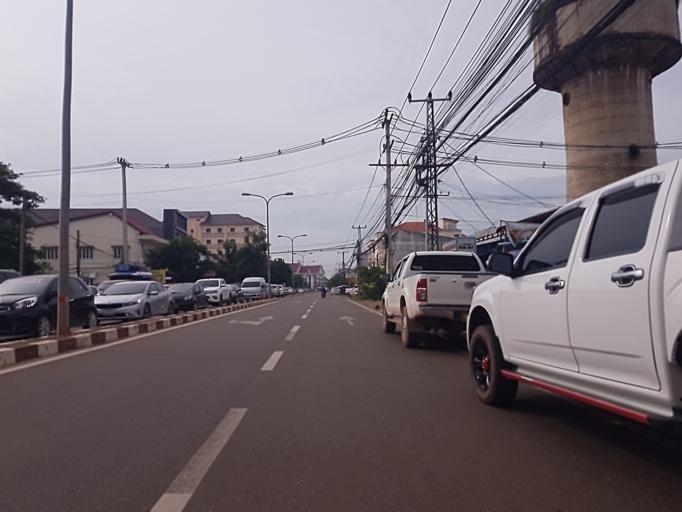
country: LA
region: Vientiane
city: Vientiane
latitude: 17.9500
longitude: 102.6193
